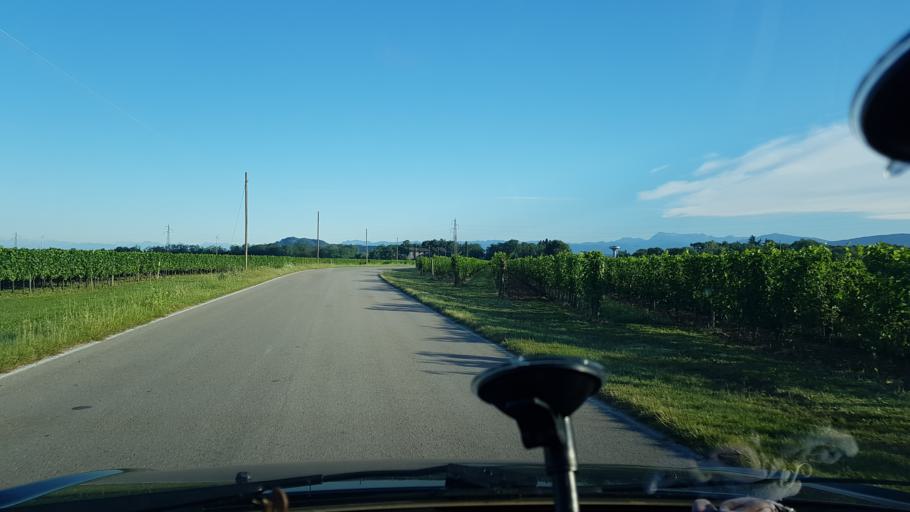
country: IT
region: Friuli Venezia Giulia
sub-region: Provincia di Gorizia
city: San Lorenzo Isontino
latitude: 45.9175
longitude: 13.5320
